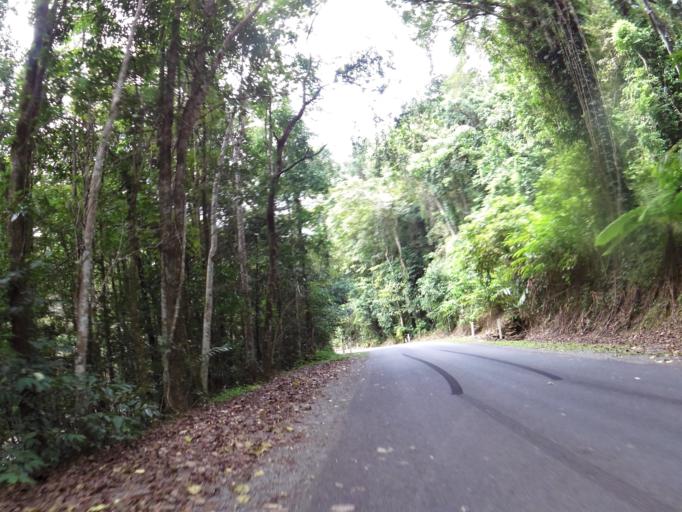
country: AU
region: Queensland
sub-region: Cairns
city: Woree
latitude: -16.9606
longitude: 145.6816
